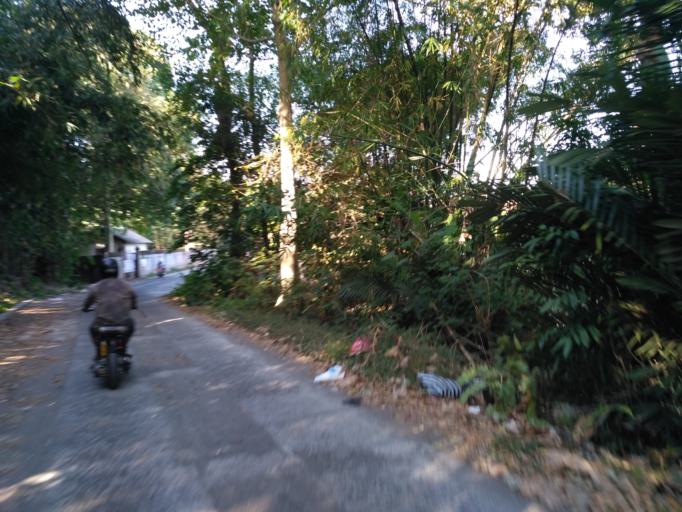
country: ID
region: Daerah Istimewa Yogyakarta
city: Depok
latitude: -7.7732
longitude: 110.4290
